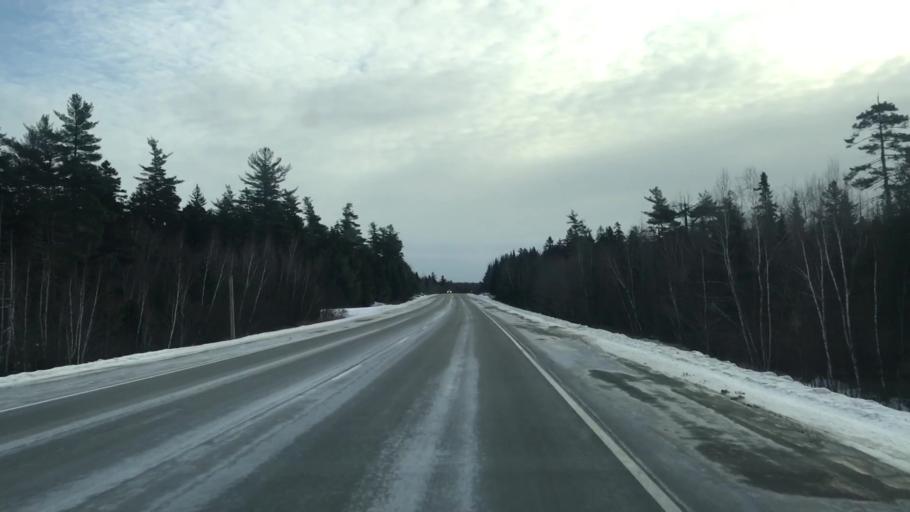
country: US
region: Maine
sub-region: Washington County
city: Addison
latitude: 44.9056
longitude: -67.8210
